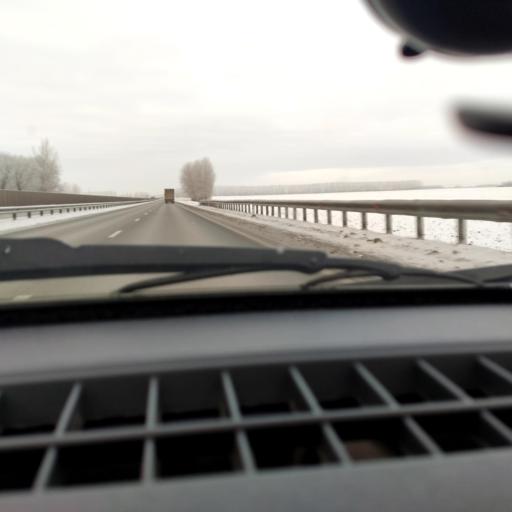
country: RU
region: Bashkortostan
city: Asanovo
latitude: 54.9872
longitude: 55.5206
